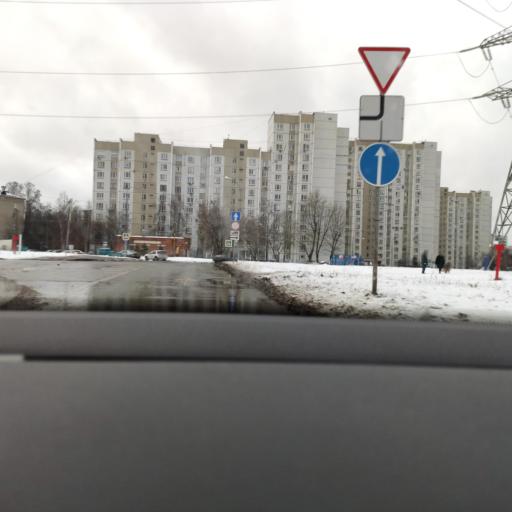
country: RU
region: Moscow
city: Metrogorodok
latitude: 55.8252
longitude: 37.7695
